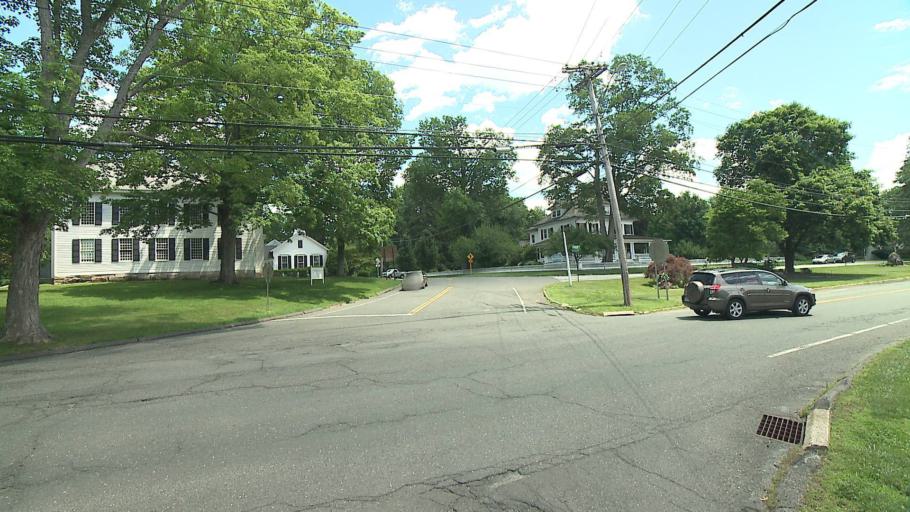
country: US
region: Connecticut
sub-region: Litchfield County
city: New Milford
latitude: 41.5351
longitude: -73.3665
